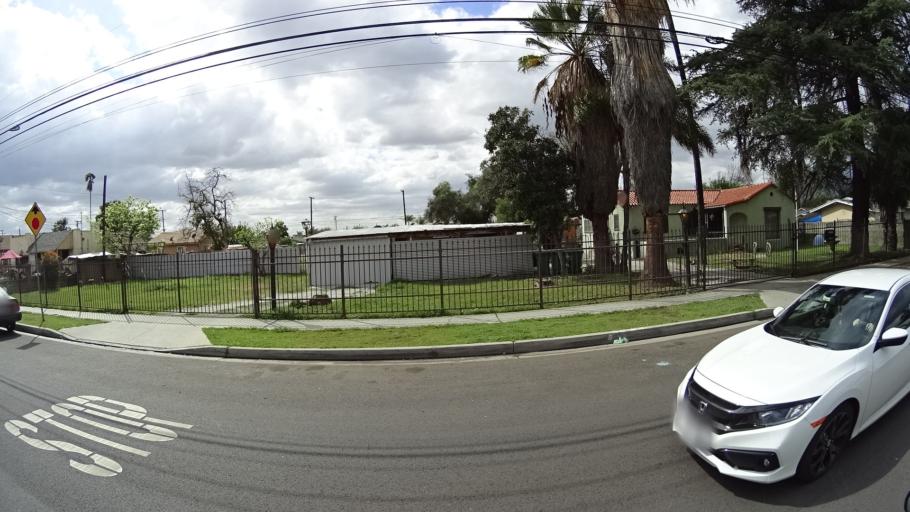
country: US
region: California
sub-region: Los Angeles County
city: Baldwin Park
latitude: 34.0896
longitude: -117.9670
